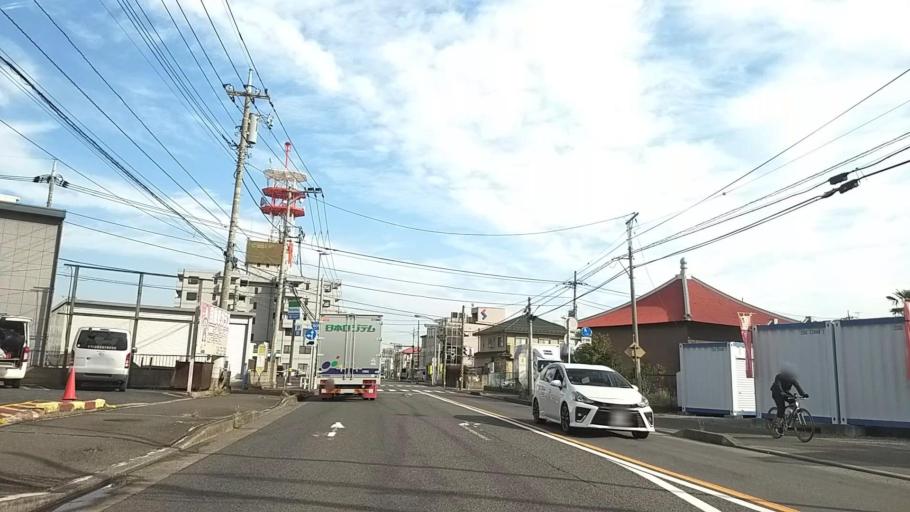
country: JP
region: Kanagawa
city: Atsugi
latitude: 35.4159
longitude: 139.3636
